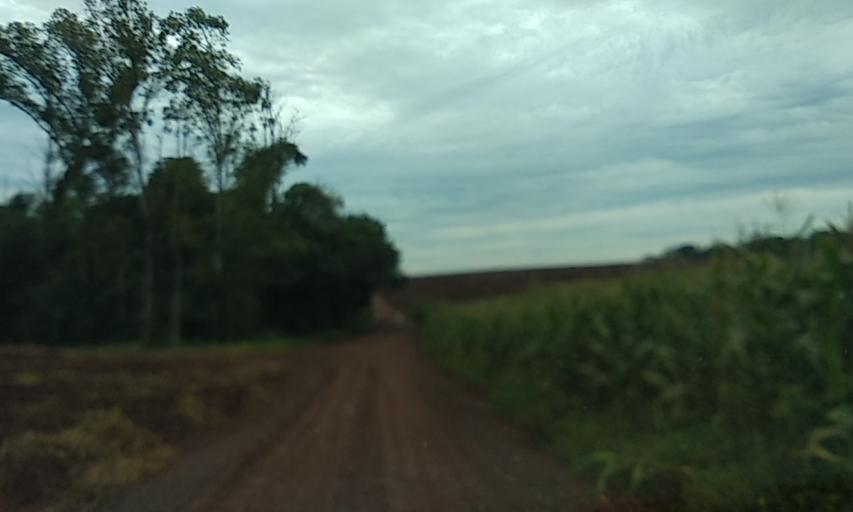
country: BR
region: Parana
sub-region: Marechal Candido Rondon
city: Marechal Candido Rondon
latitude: -24.5310
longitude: -54.0875
